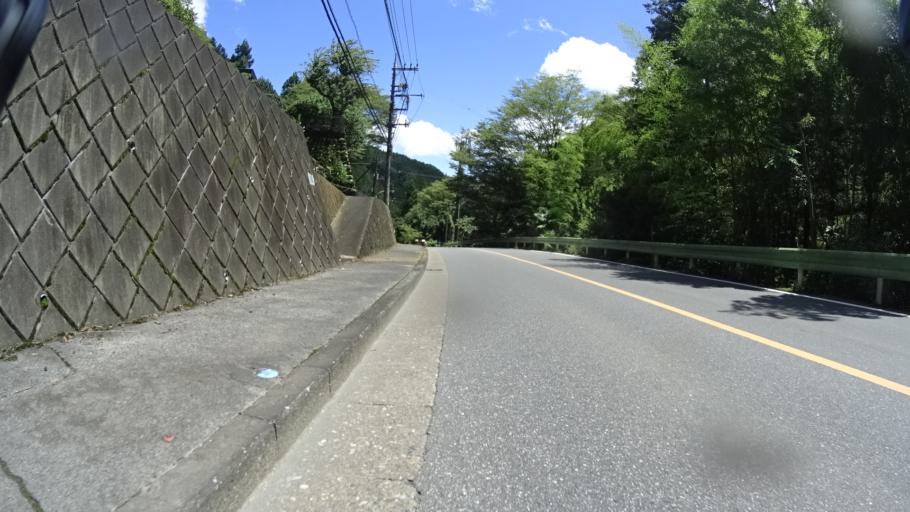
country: JP
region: Tokyo
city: Ome
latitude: 35.8254
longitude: 139.2219
